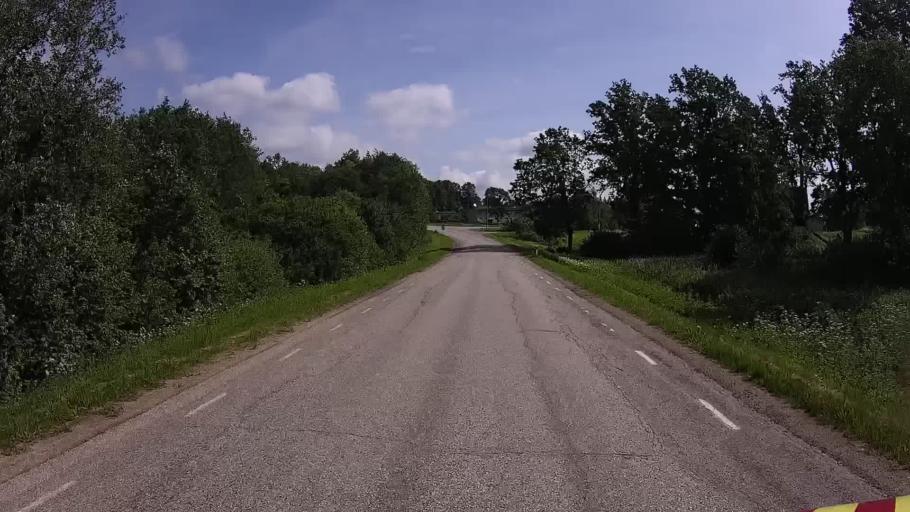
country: EE
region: Vorumaa
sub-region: Antsla vald
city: Vana-Antsla
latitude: 57.8600
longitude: 26.6060
